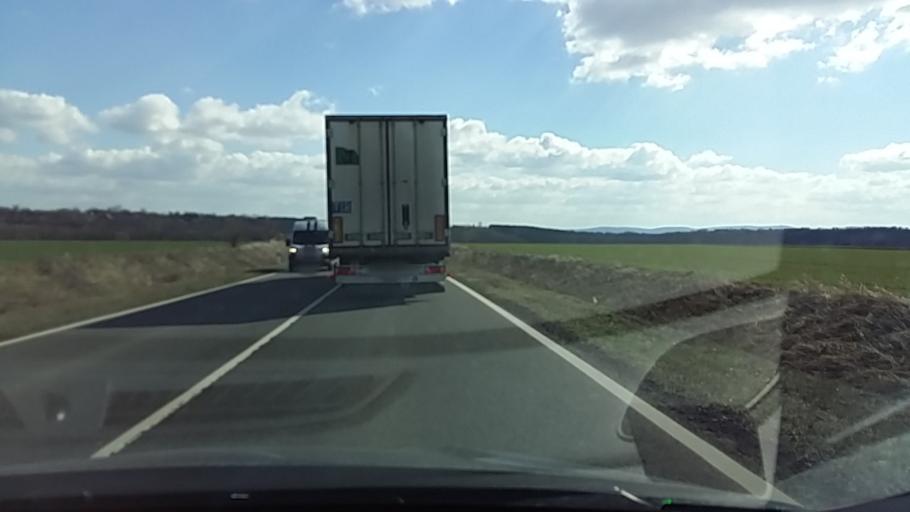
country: HU
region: Baranya
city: Kozarmisleny
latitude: 46.0324
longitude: 18.2740
